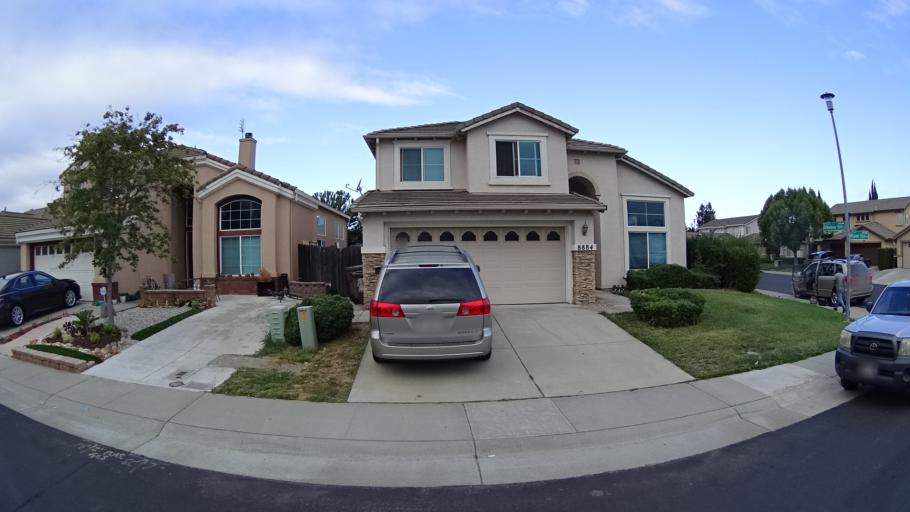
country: US
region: California
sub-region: Sacramento County
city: Laguna
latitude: 38.4346
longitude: -121.4248
